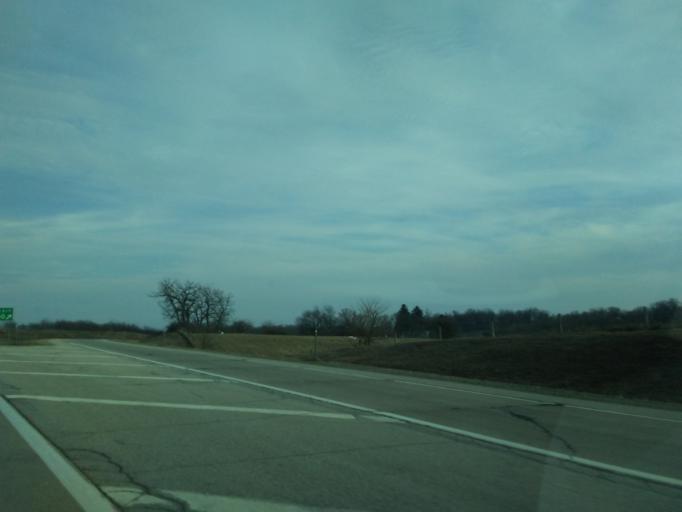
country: US
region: Wisconsin
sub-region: Iowa County
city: Dodgeville
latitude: 42.9665
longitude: -90.1073
